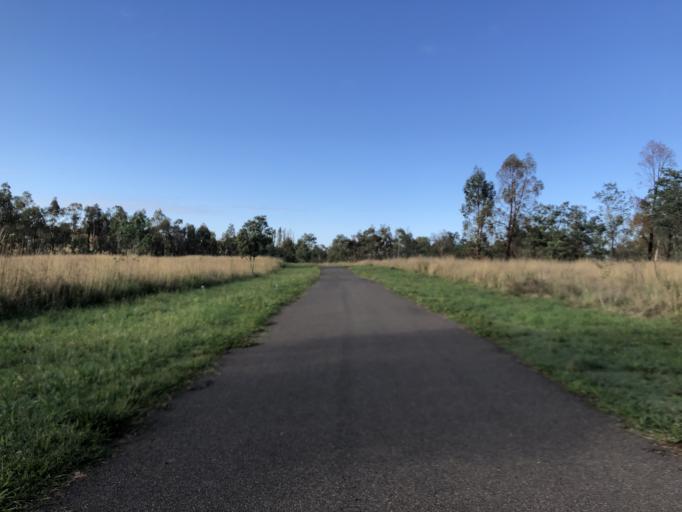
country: AU
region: New South Wales
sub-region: Orange Municipality
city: Orange
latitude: -33.3279
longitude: 149.0850
